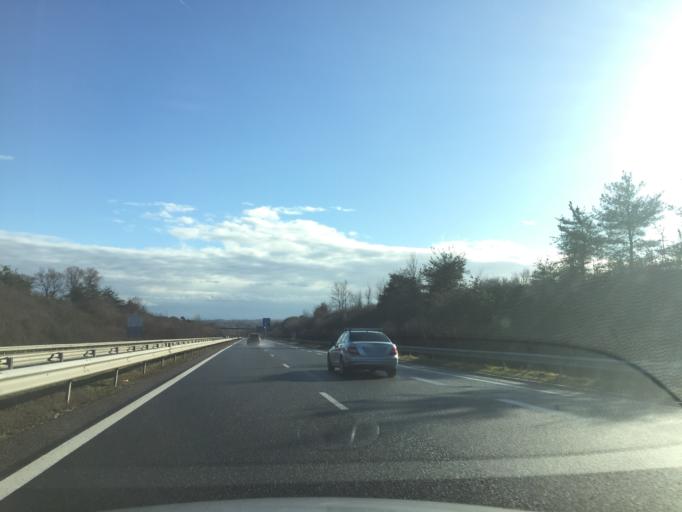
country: FR
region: Rhone-Alpes
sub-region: Departement de la Loire
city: Saint-Germain-Laval
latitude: 45.8365
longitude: 4.0959
